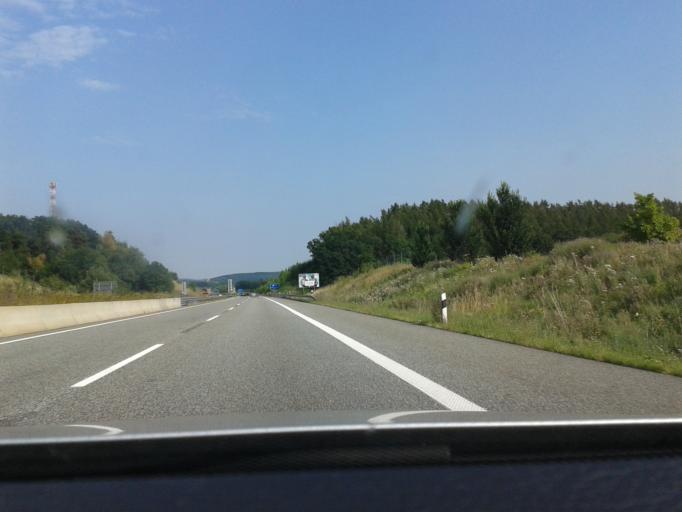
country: DE
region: Thuringia
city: Rustenfelde
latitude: 51.4033
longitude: 10.0125
